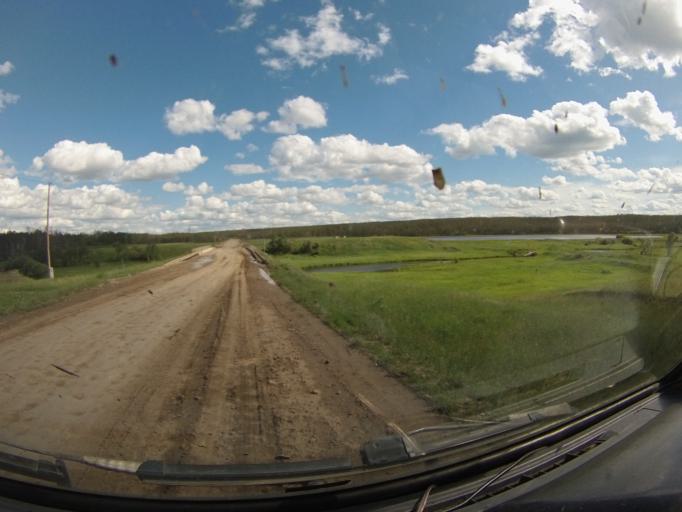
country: RU
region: Sakha
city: Churapcha
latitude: 61.9577
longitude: 132.0690
